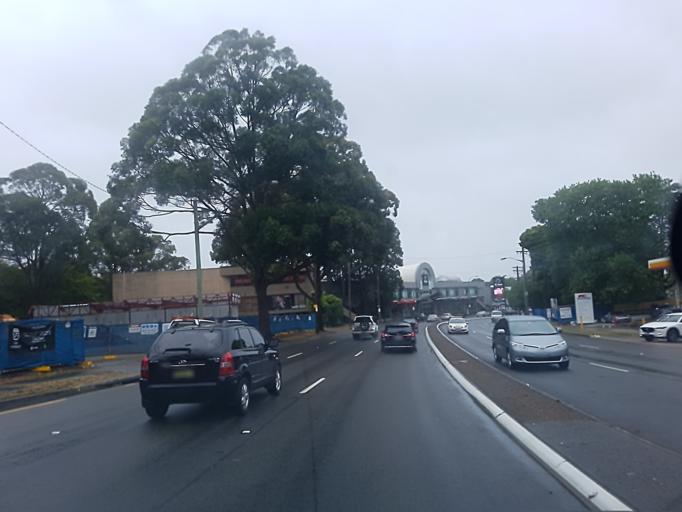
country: AU
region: New South Wales
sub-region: City of Sydney
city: Pymble
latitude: -33.7313
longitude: 151.1568
